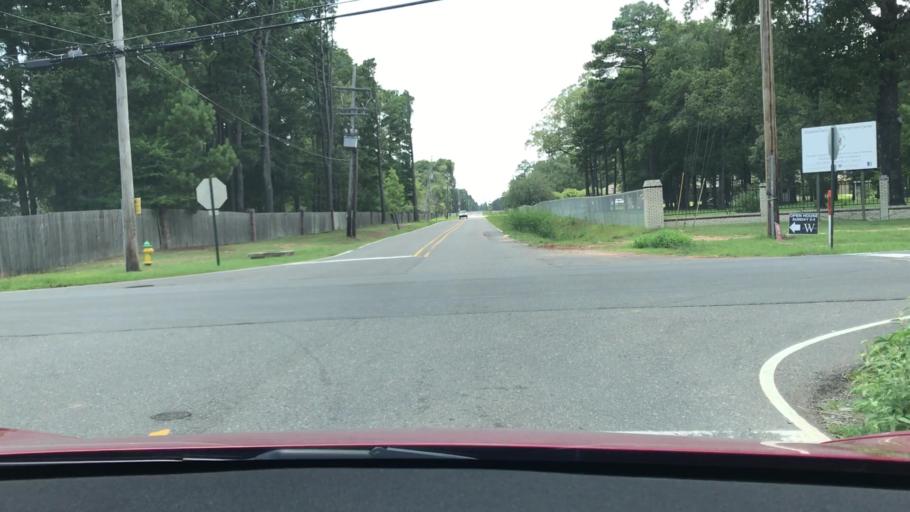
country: US
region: Louisiana
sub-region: De Soto Parish
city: Stonewall
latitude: 32.3693
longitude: -93.7137
